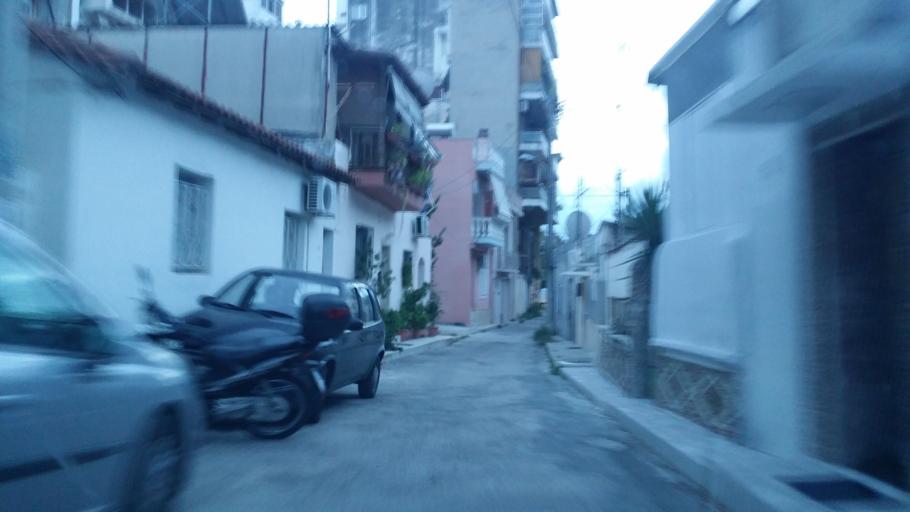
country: GR
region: Attica
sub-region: Nomarchia Athinas
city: Nea Ionia
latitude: 38.0438
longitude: 23.7476
